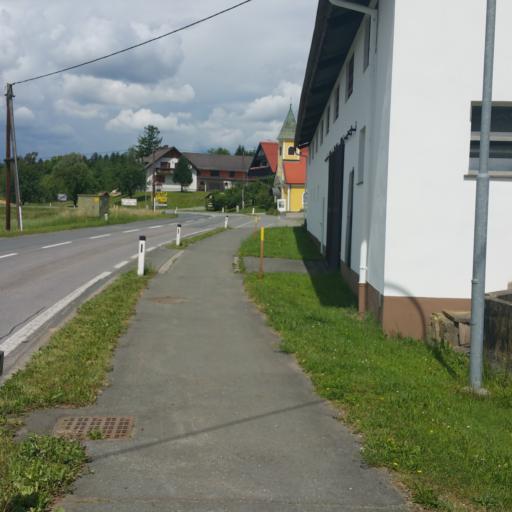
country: AT
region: Styria
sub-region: Politischer Bezirk Deutschlandsberg
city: Sankt Martin im Sulmtal
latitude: 46.7497
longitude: 15.3307
